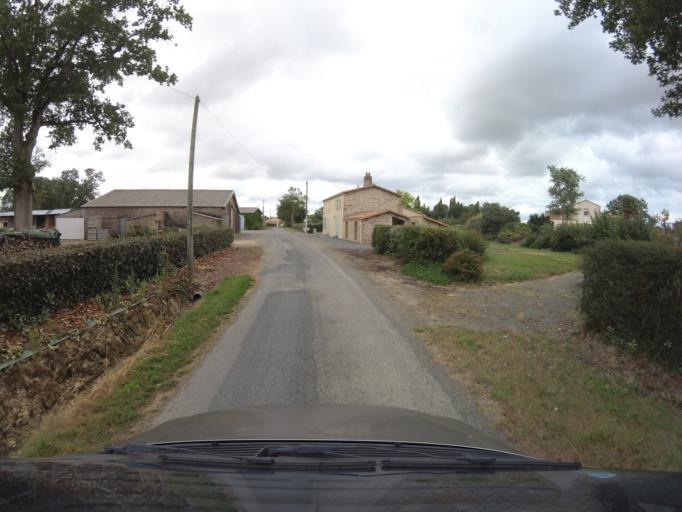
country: FR
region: Pays de la Loire
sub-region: Departement de la Vendee
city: Saint-Philbert-de-Bouaine
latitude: 46.9913
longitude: -1.4868
